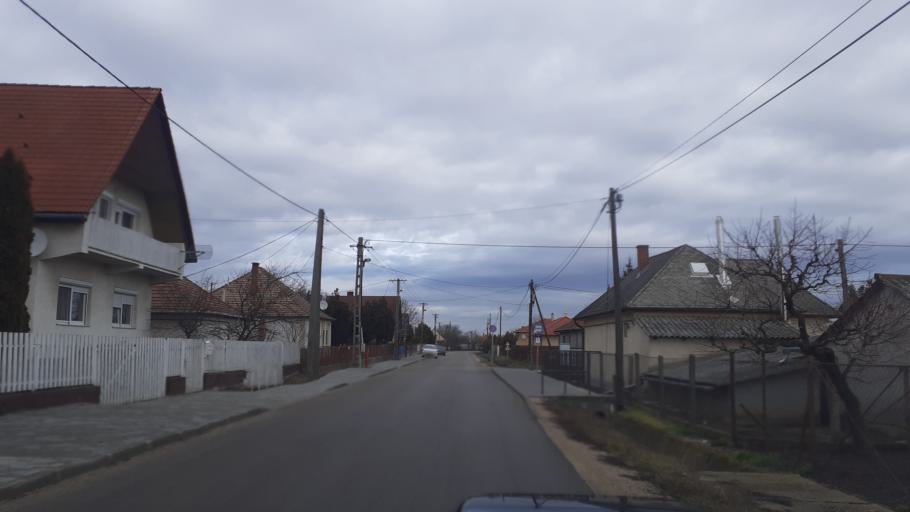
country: HU
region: Fejer
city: Pakozd
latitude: 47.1656
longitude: 18.5182
